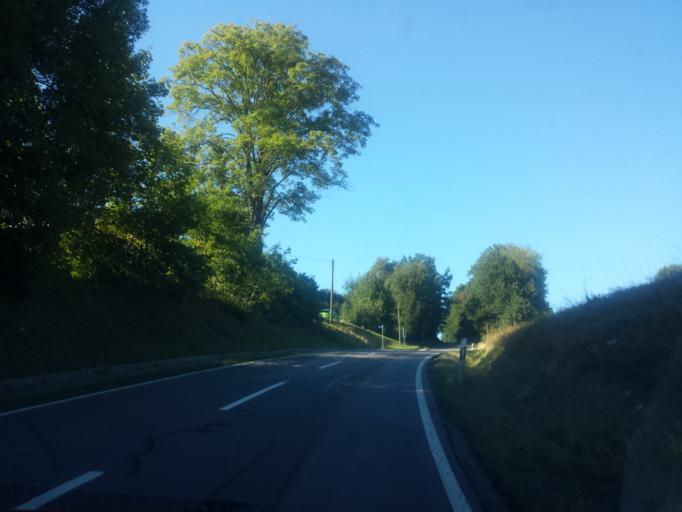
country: DE
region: Bavaria
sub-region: Lower Bavaria
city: Viechtach
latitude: 49.0893
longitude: 12.8867
